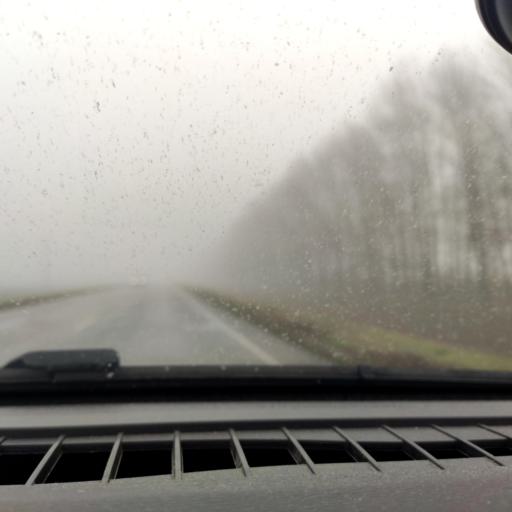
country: RU
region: Belgorod
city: Ilovka
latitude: 50.7477
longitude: 38.7135
